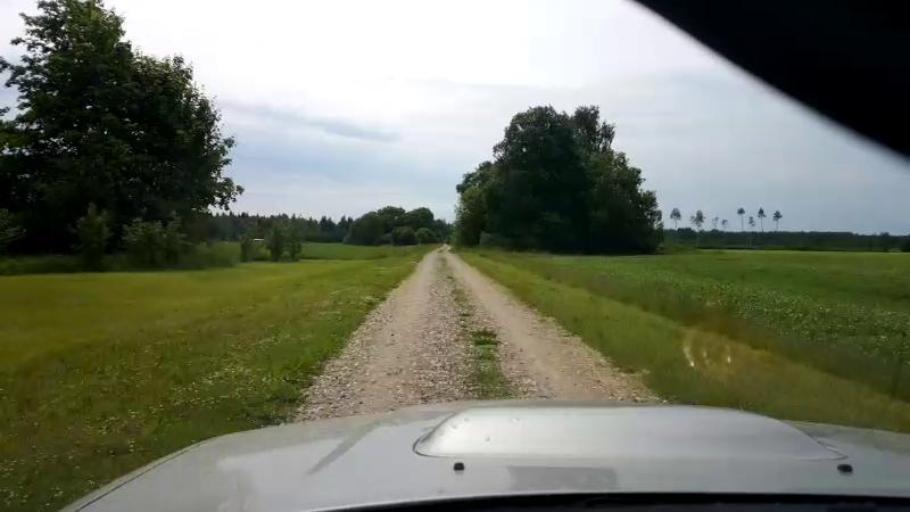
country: EE
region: Paernumaa
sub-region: Tootsi vald
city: Tootsi
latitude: 58.5597
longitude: 24.7509
